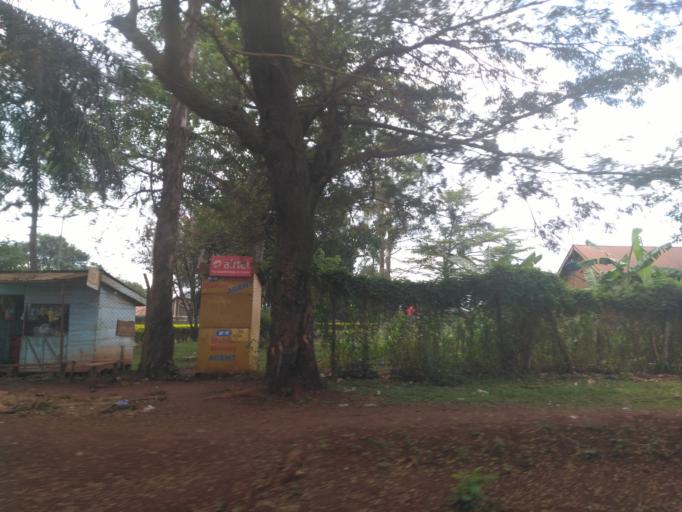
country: UG
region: Central Region
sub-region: Buikwe District
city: Njeru
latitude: 0.4242
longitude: 33.1891
